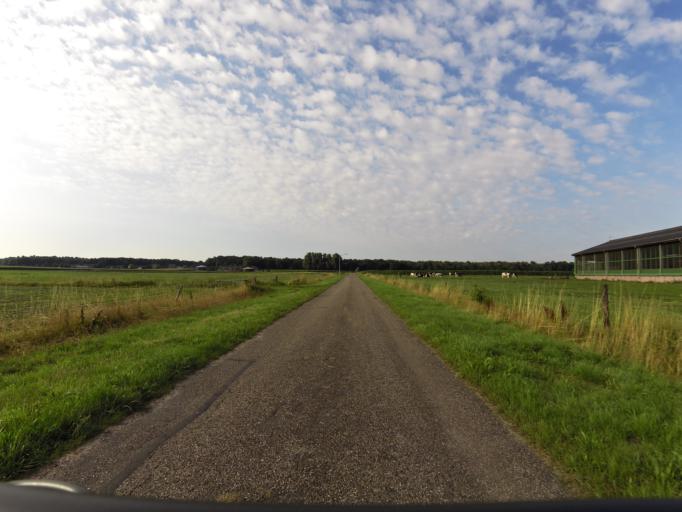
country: NL
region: North Brabant
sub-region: Gemeente Woensdrecht
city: Woensdrecht
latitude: 51.4460
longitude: 4.3718
